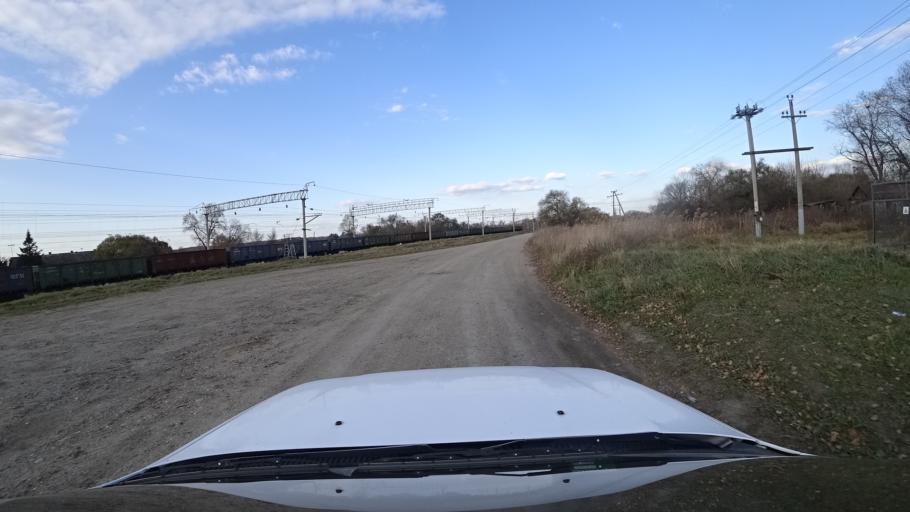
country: RU
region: Primorskiy
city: Lazo
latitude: 45.8215
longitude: 133.6124
